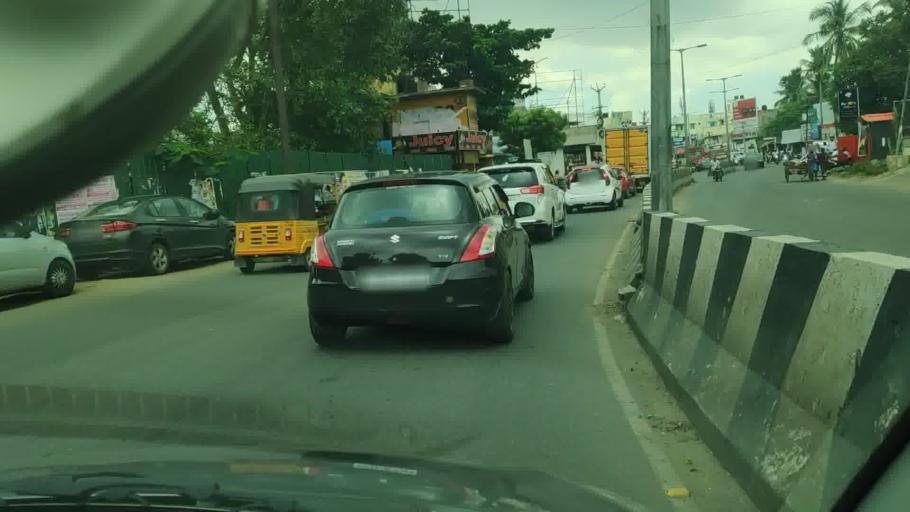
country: IN
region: Tamil Nadu
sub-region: Thiruvallur
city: Ambattur
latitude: 13.1129
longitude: 80.1502
